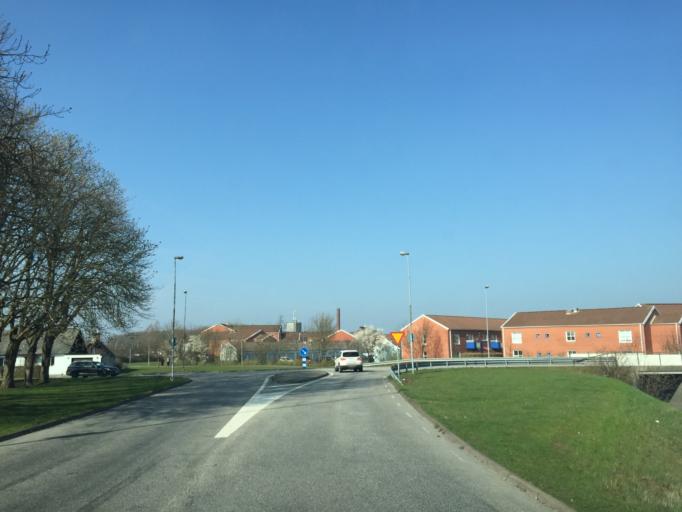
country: SE
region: Skane
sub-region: Staffanstorps Kommun
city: Staffanstorp
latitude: 55.6369
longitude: 13.2178
